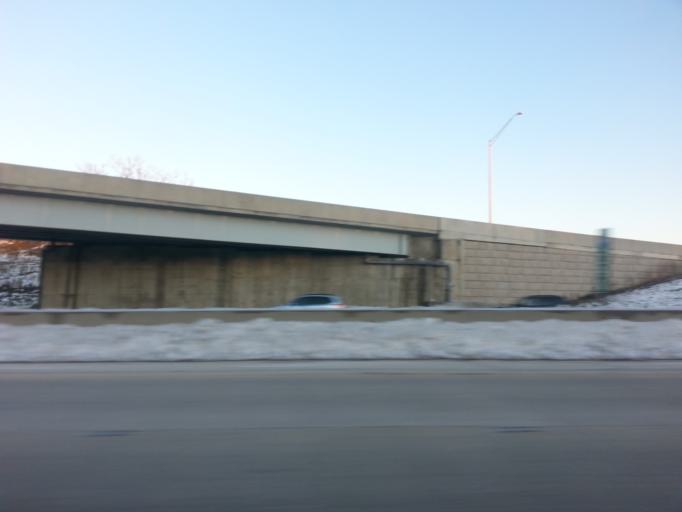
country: US
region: Illinois
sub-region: DuPage County
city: Oak Brook
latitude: 41.8437
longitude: -87.9195
